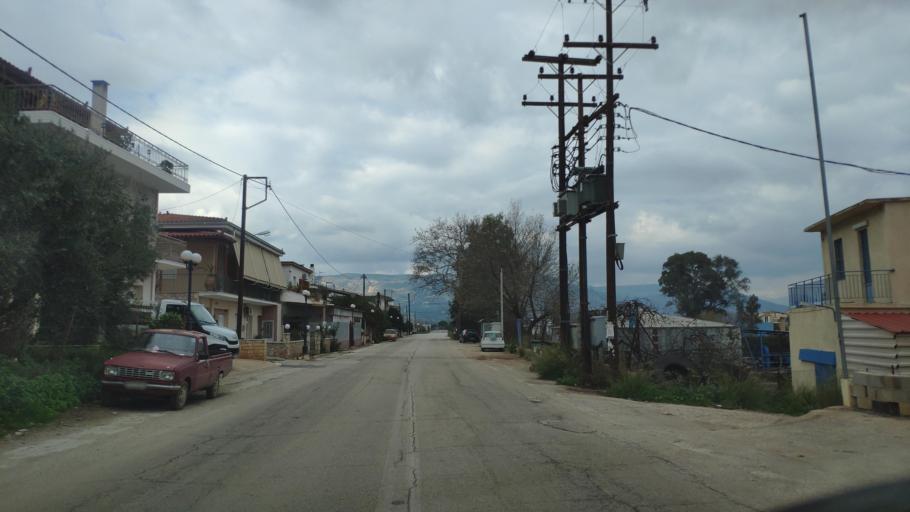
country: GR
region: Peloponnese
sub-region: Nomos Argolidos
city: Nea Kios
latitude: 37.5571
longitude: 22.7137
